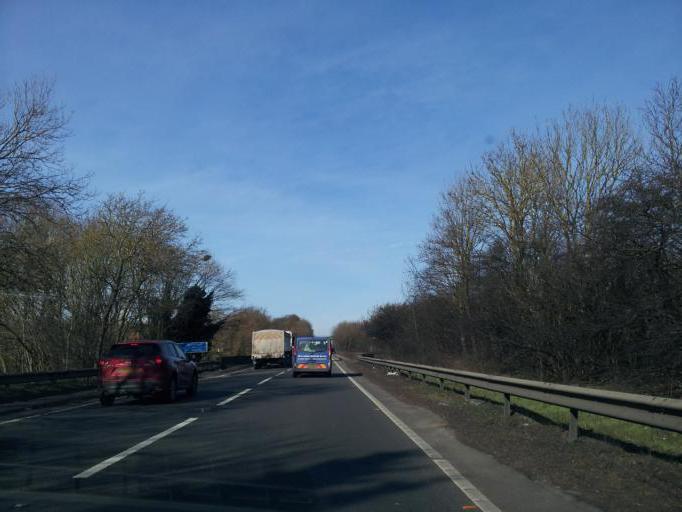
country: GB
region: England
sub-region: Peterborough
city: Wansford
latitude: 52.5806
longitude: -0.4125
